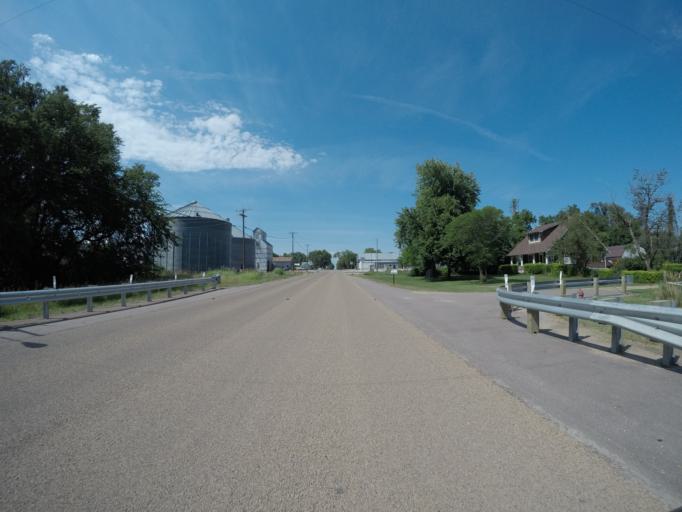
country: US
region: Nebraska
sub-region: Webster County
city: Red Cloud
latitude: 40.0695
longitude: -98.3303
